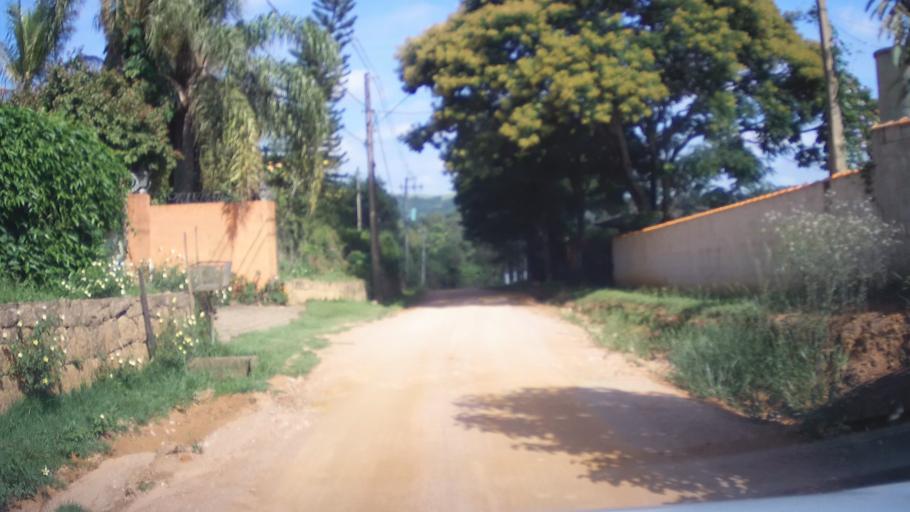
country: BR
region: Sao Paulo
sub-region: Itupeva
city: Itupeva
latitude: -23.2183
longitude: -47.0716
